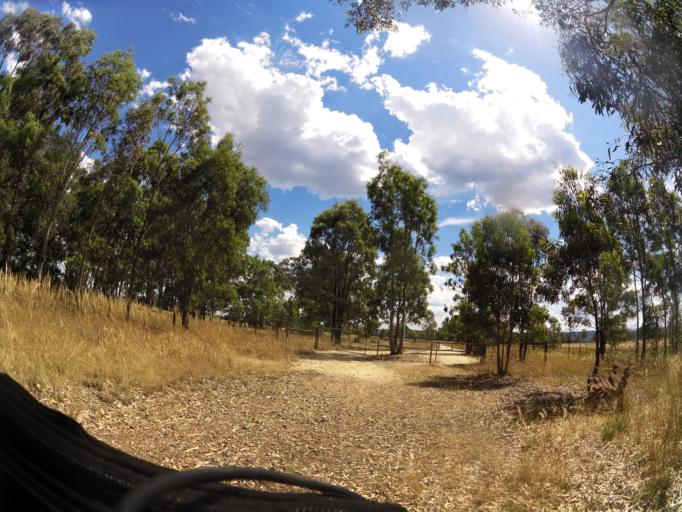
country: AU
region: Victoria
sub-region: Wellington
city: Heyfield
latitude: -37.9836
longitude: 146.7244
